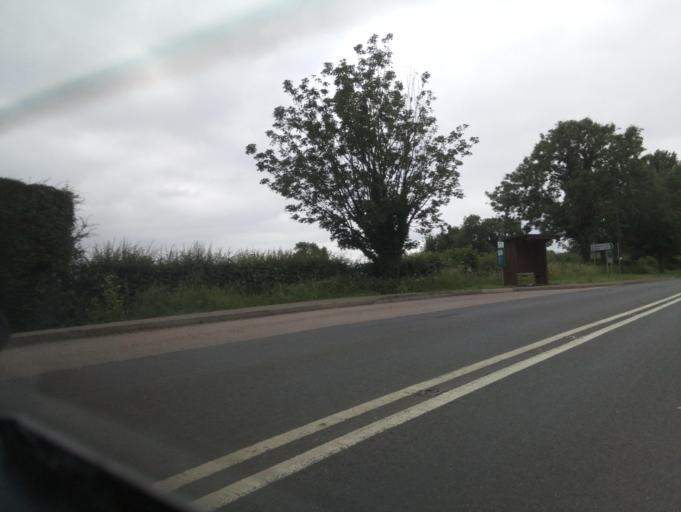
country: GB
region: England
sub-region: District of Rutland
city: Preston
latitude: 52.6114
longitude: -0.7134
